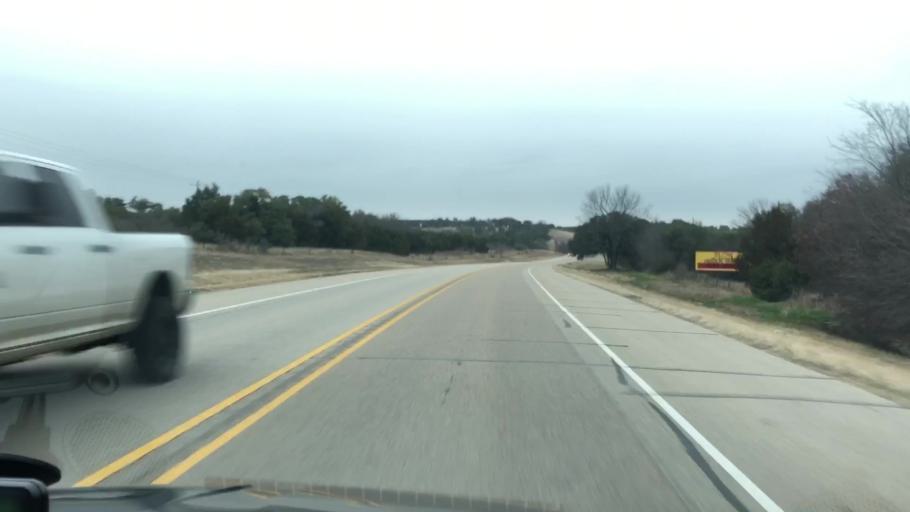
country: US
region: Texas
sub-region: Hamilton County
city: Hamilton
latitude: 31.7630
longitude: -98.1224
